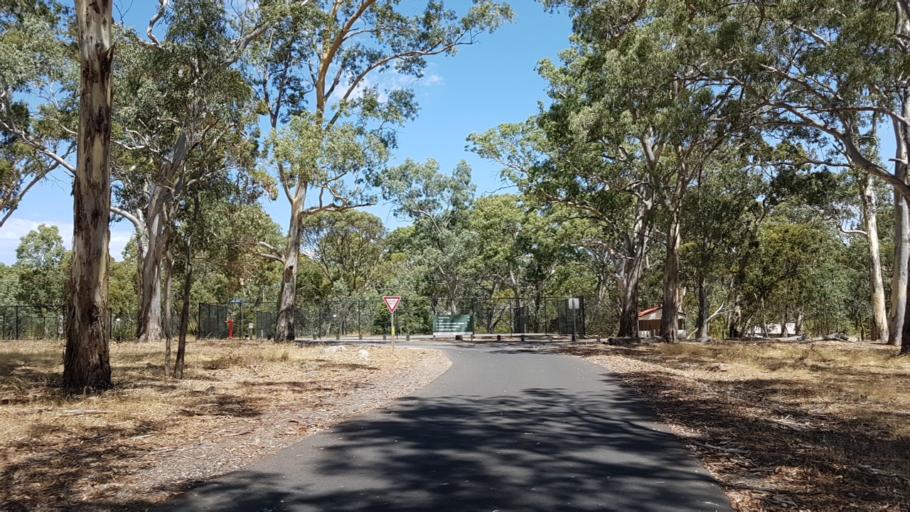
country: AU
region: South Australia
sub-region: Mitcham
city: Belair
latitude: -35.0082
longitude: 138.6373
